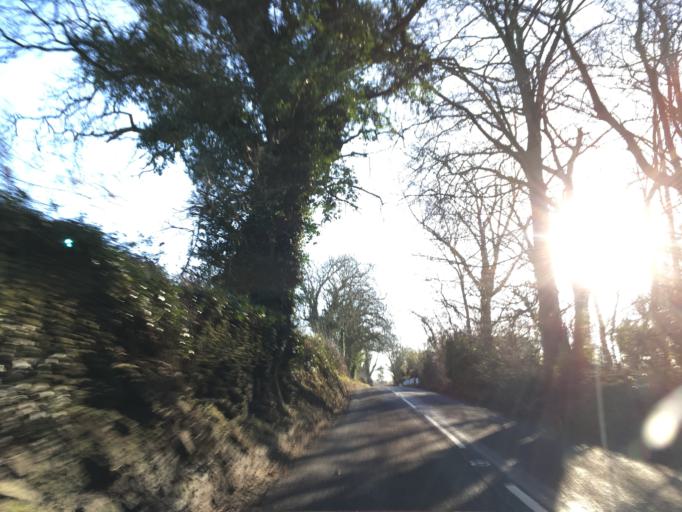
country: GB
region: England
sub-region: Wiltshire
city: Nettleton
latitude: 51.5049
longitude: -2.2281
